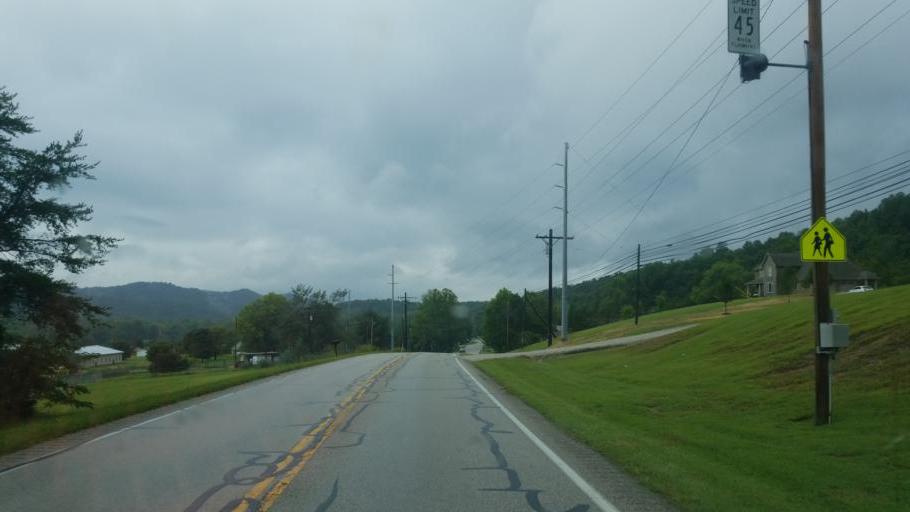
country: US
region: Kentucky
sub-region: Rowan County
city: Morehead
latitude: 38.1572
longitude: -83.4604
